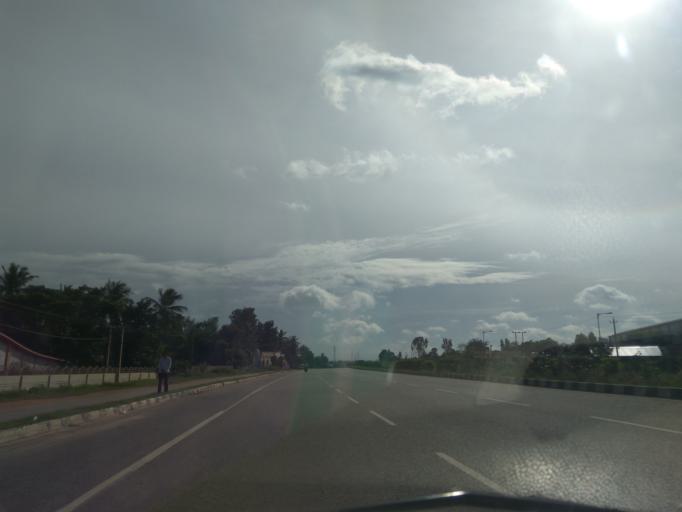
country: IN
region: Karnataka
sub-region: Bangalore Rural
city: Hoskote
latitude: 13.0819
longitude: 77.8162
